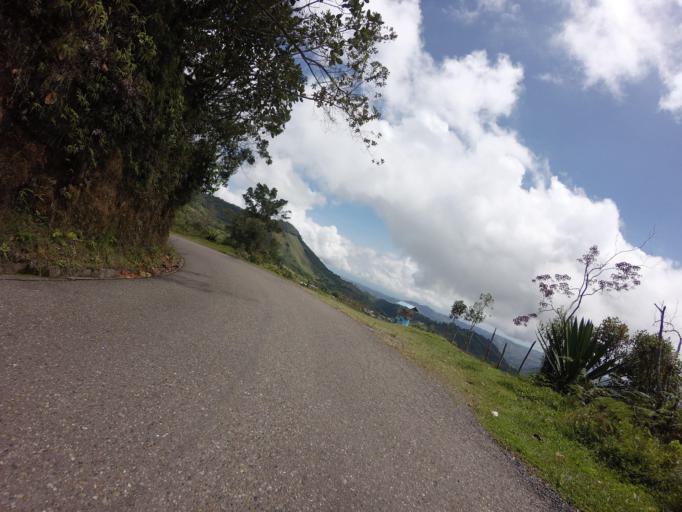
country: CO
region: Caldas
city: Manzanares
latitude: 5.2735
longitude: -75.1182
